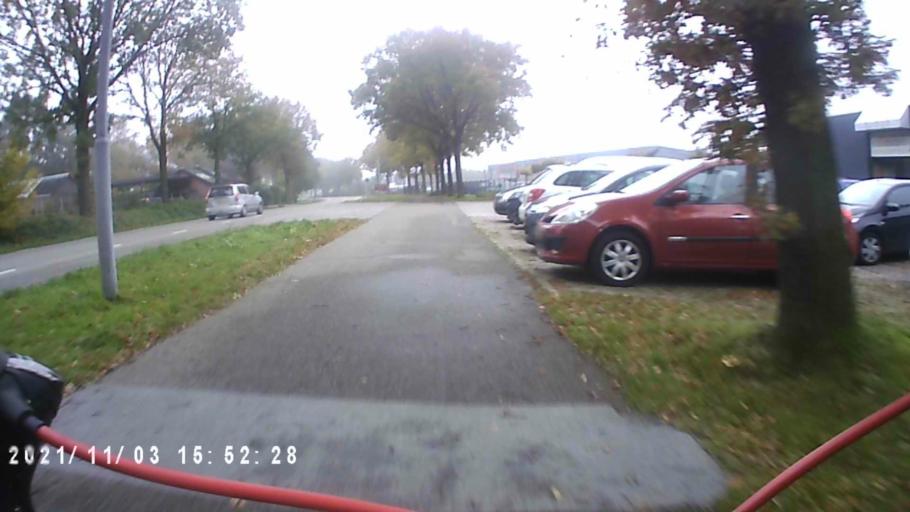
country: NL
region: Groningen
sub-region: Gemeente Leek
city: Leek
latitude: 53.0747
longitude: 6.3321
